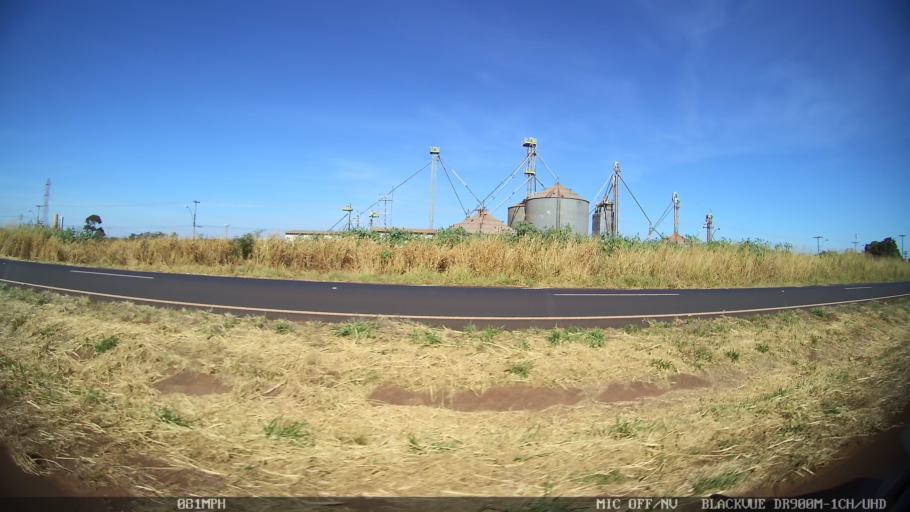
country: BR
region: Sao Paulo
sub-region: Barretos
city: Barretos
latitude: -20.5135
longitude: -48.5648
